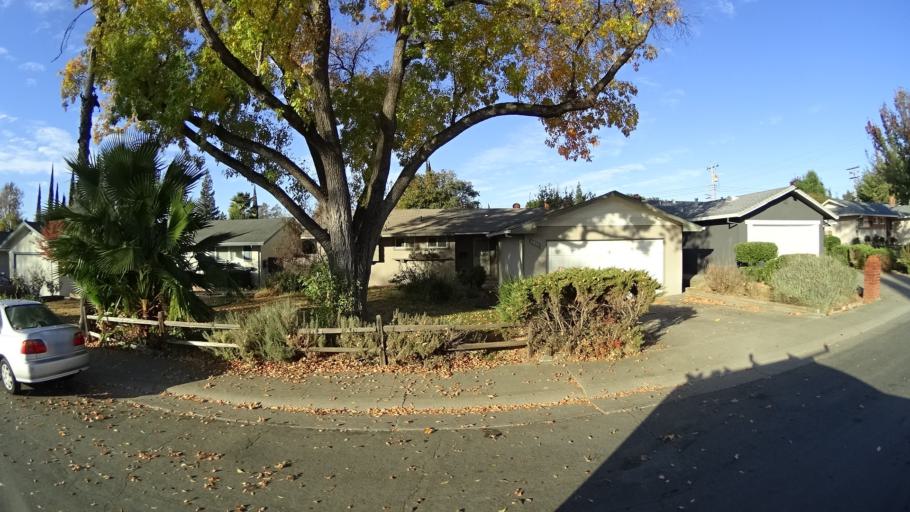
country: US
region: California
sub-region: Sacramento County
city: Citrus Heights
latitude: 38.6774
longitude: -121.3035
